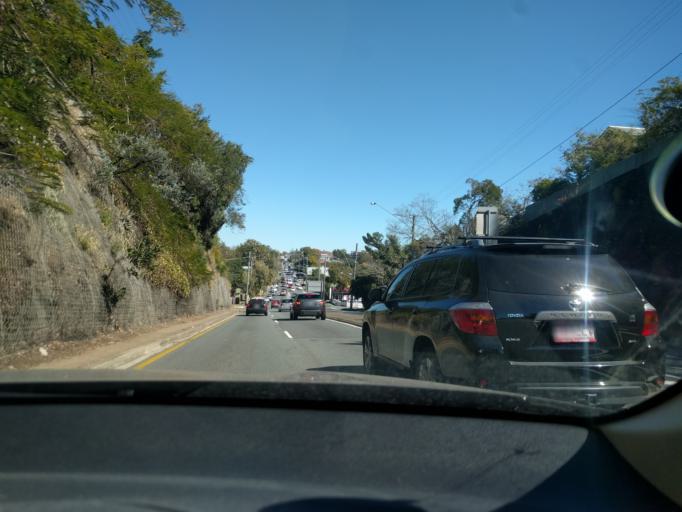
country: AU
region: Queensland
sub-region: Brisbane
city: Toowong
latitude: -27.4750
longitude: 152.9941
